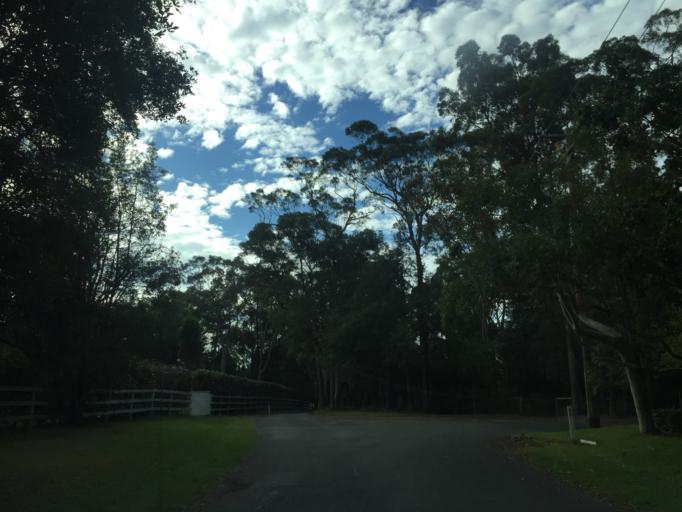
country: AU
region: New South Wales
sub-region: Hornsby Shire
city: Galston
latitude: -33.6459
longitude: 151.0752
